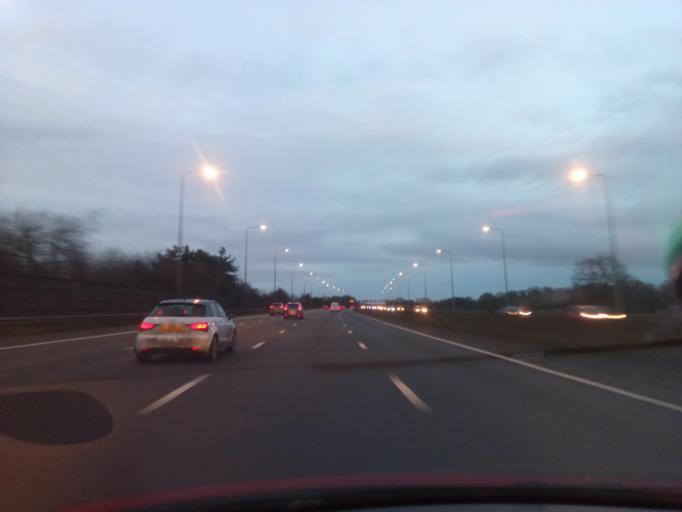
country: GB
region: England
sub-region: Nottinghamshire
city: Kimberley
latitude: 52.9514
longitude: -1.2769
